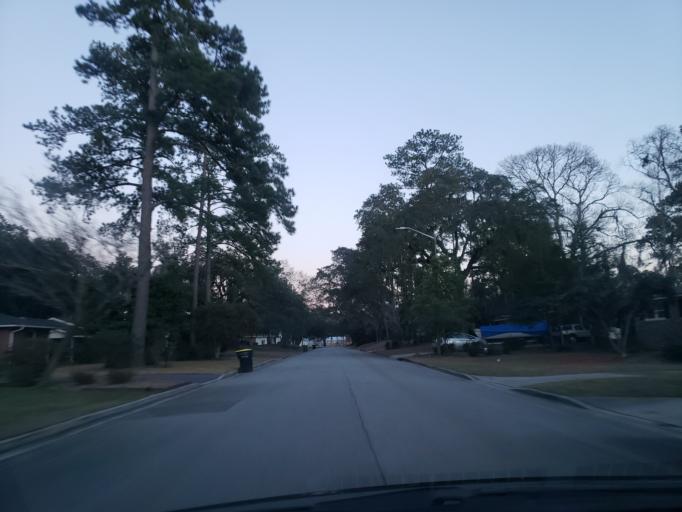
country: US
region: Georgia
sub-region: Chatham County
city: Thunderbolt
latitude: 32.0189
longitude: -81.0778
